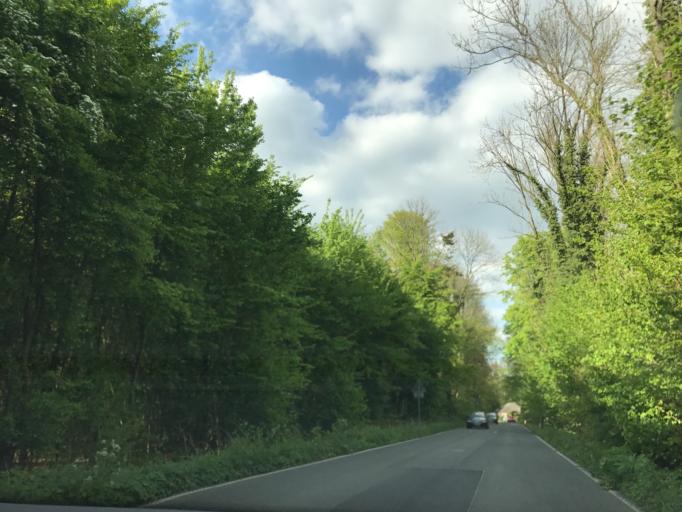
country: DE
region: North Rhine-Westphalia
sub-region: Regierungsbezirk Dusseldorf
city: Heiligenhaus
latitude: 51.3635
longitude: 6.9597
